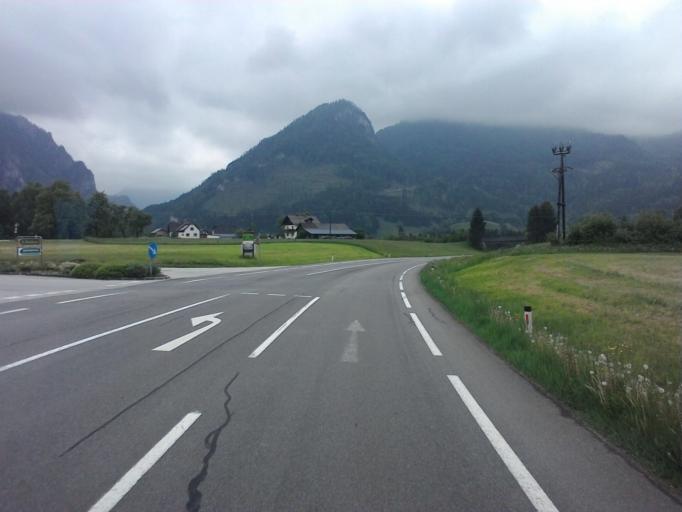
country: AT
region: Styria
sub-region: Politischer Bezirk Liezen
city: Gams bei Hieflau
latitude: 47.6493
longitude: 14.7628
